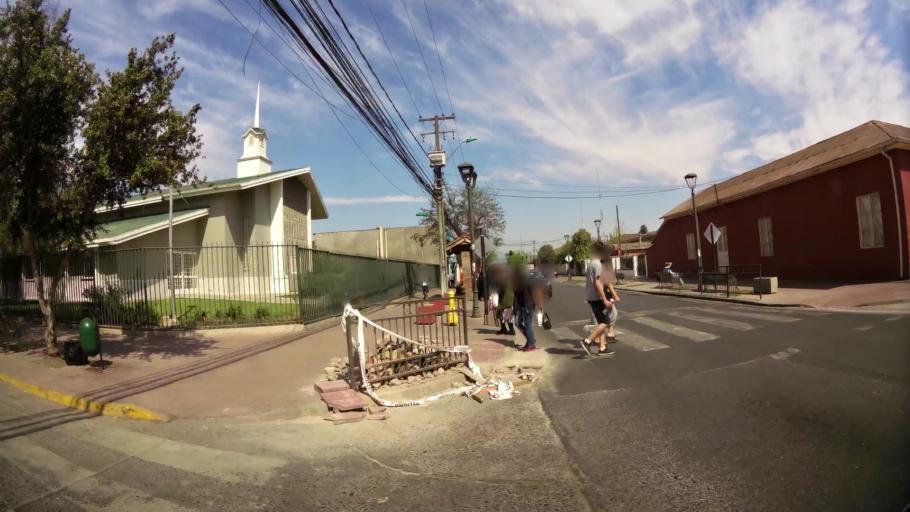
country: CL
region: Santiago Metropolitan
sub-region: Provincia de Talagante
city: Talagante
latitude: -33.6651
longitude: -70.9285
